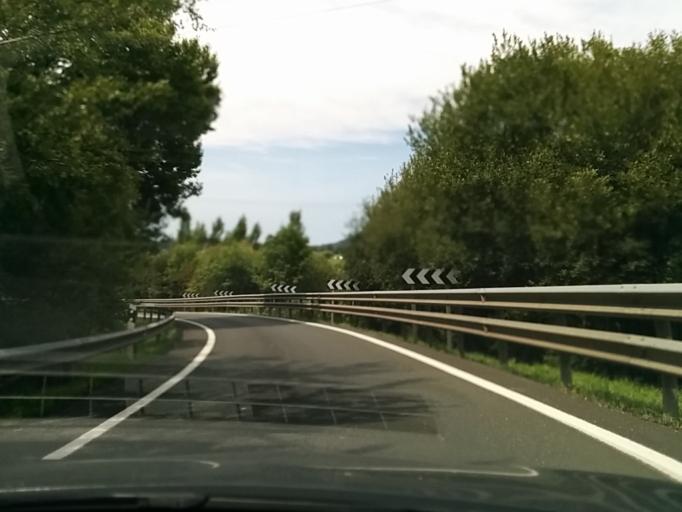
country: ES
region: Basque Country
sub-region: Provincia de Guipuzcoa
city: Irun
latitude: 43.3475
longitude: -1.8121
